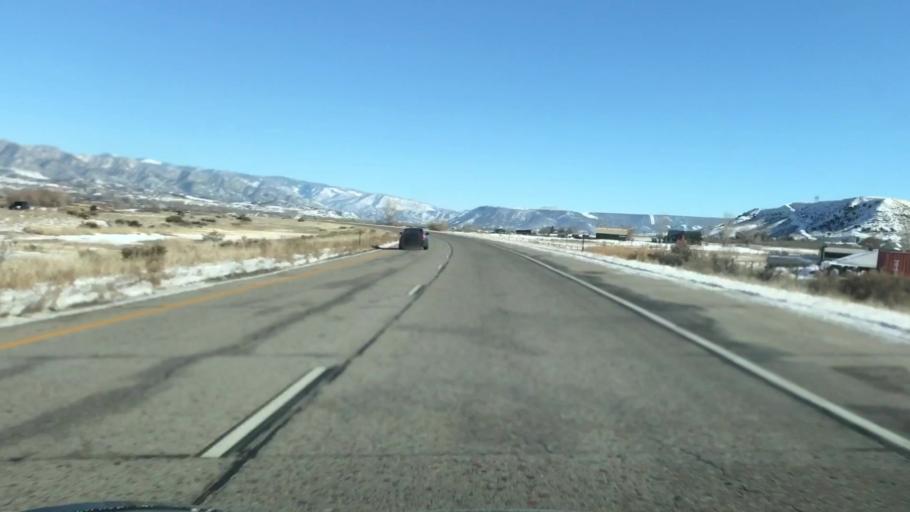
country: US
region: Colorado
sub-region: Garfield County
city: Silt
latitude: 39.5326
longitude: -107.7000
